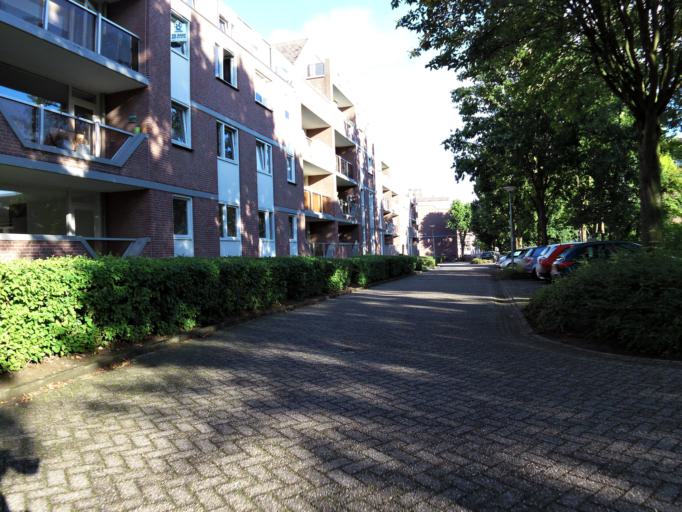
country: NL
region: Limburg
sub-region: Gemeente Heerlen
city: Heerlen
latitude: 50.8703
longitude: 5.9799
